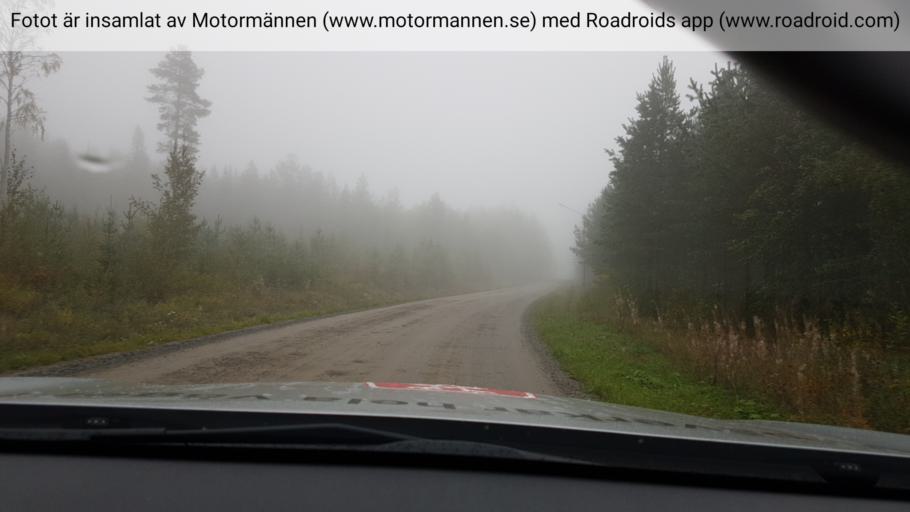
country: SE
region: Vaesterbotten
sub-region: Umea Kommun
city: Ersmark
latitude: 64.0880
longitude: 20.2038
